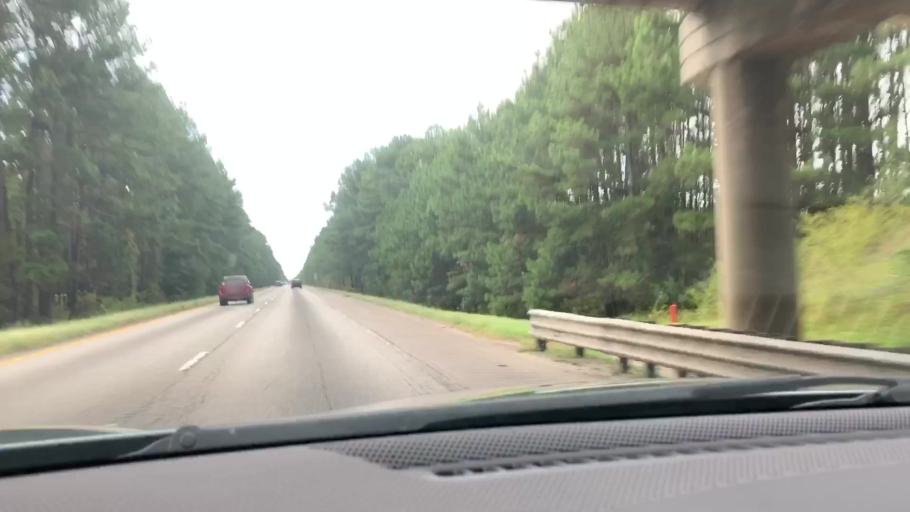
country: US
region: South Carolina
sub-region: Orangeburg County
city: Holly Hill
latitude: 33.3254
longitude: -80.5543
